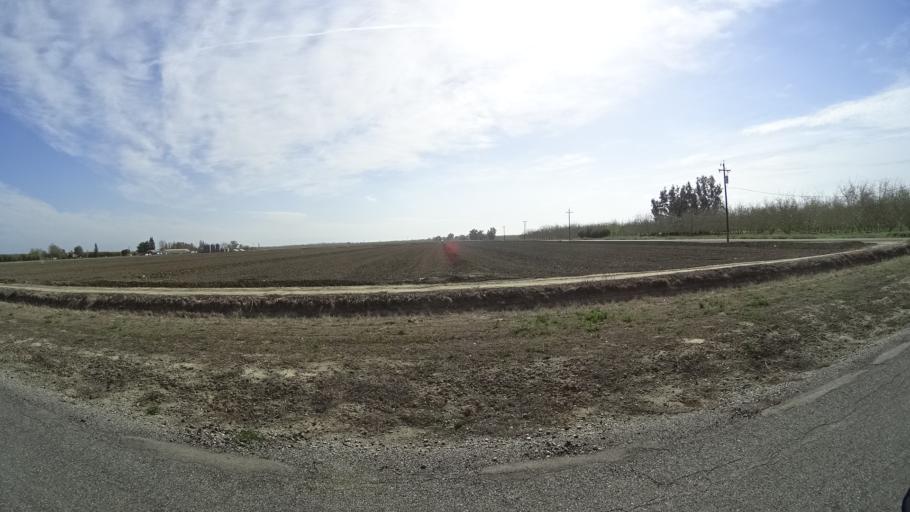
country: US
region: California
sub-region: Glenn County
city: Hamilton City
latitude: 39.6239
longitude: -122.0463
